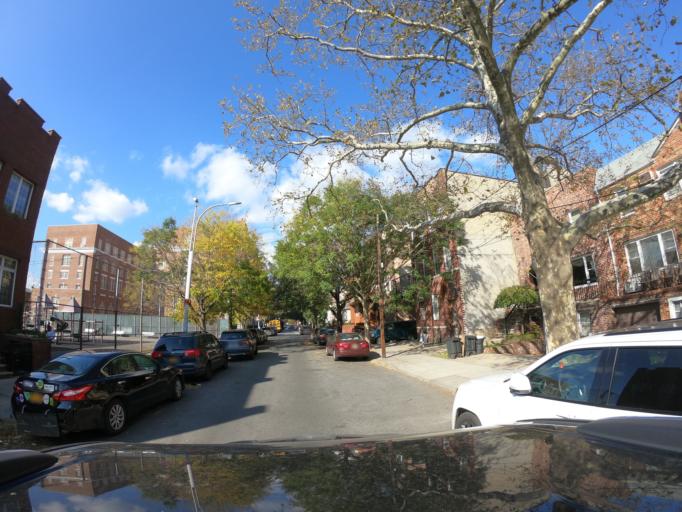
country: US
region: New York
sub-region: Kings County
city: Bensonhurst
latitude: 40.6264
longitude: -73.9883
